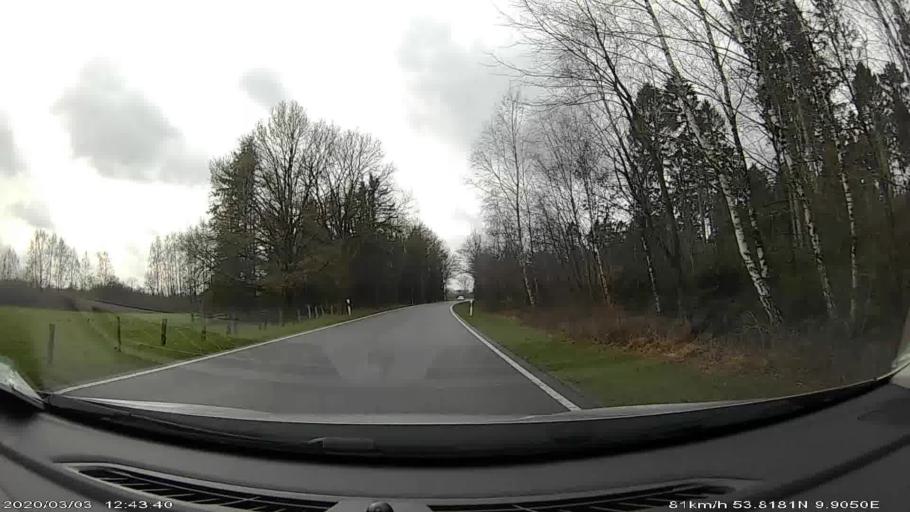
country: DE
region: Schleswig-Holstein
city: Alveslohe
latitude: 53.8168
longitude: 9.9025
